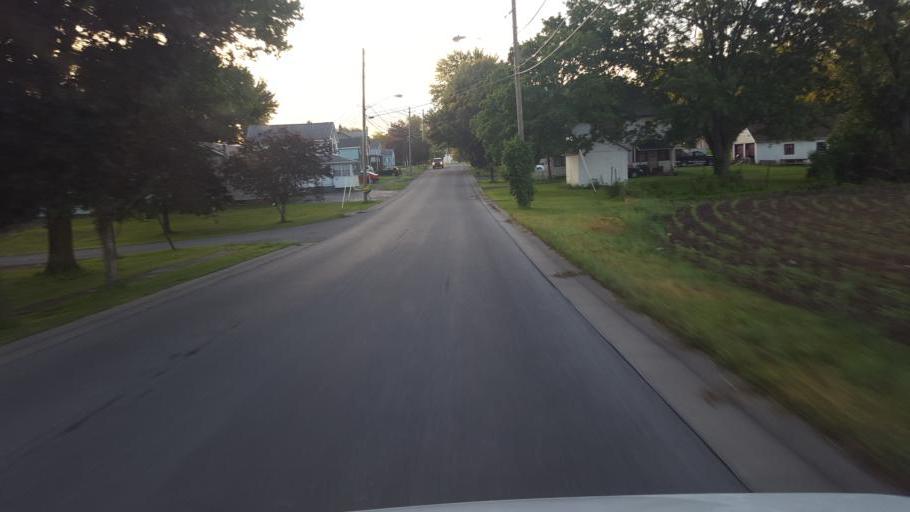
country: US
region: New York
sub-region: Wayne County
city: Clyde
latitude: 43.0810
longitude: -76.8771
